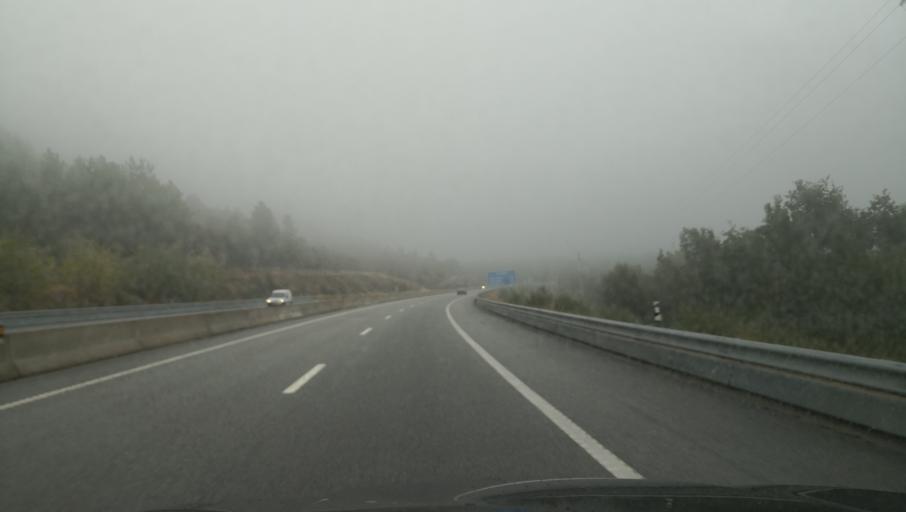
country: PT
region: Vila Real
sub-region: Sabrosa
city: Sabrosa
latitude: 41.3316
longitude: -7.6254
